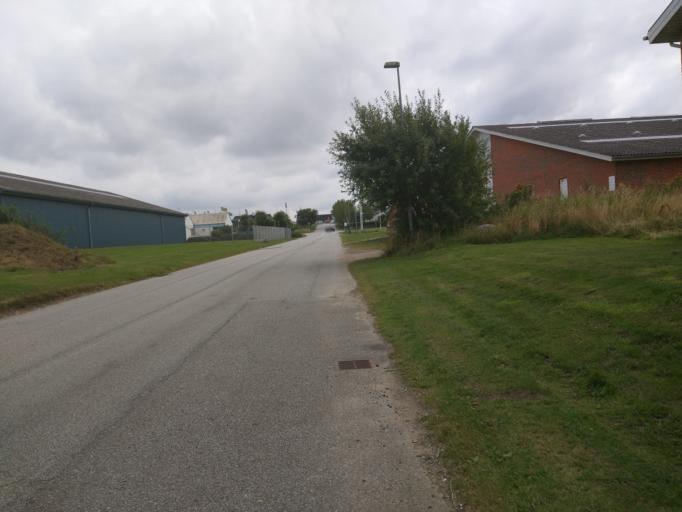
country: DK
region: Central Jutland
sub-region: Viborg Kommune
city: Viborg
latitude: 56.4503
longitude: 9.3648
